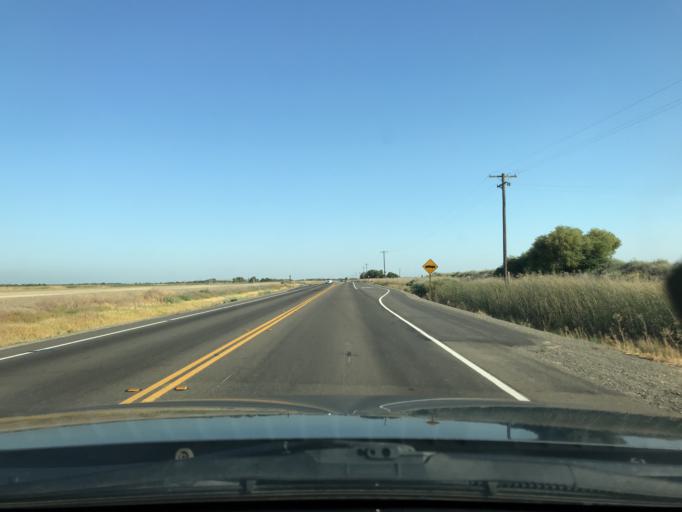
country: US
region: California
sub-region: Merced County
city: Los Banos
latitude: 37.1948
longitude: -120.8407
